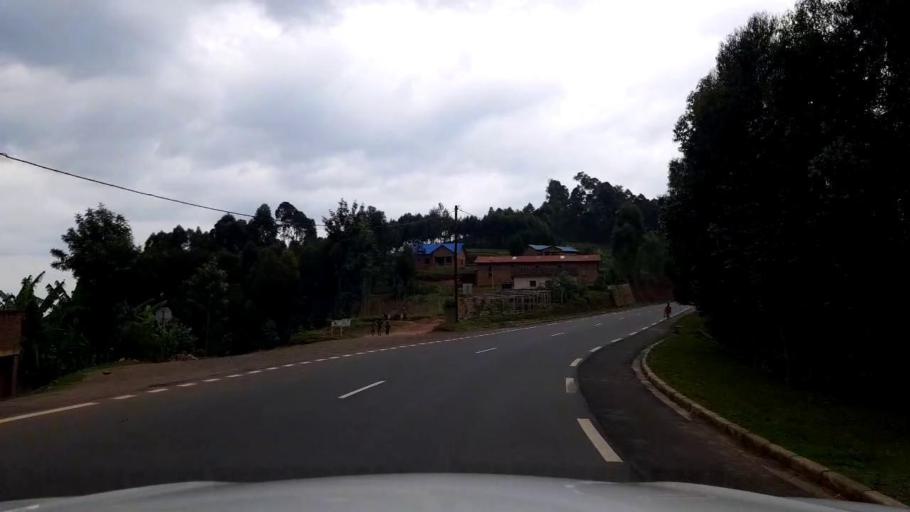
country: RW
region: Western Province
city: Kibuye
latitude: -1.8892
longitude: 29.3454
